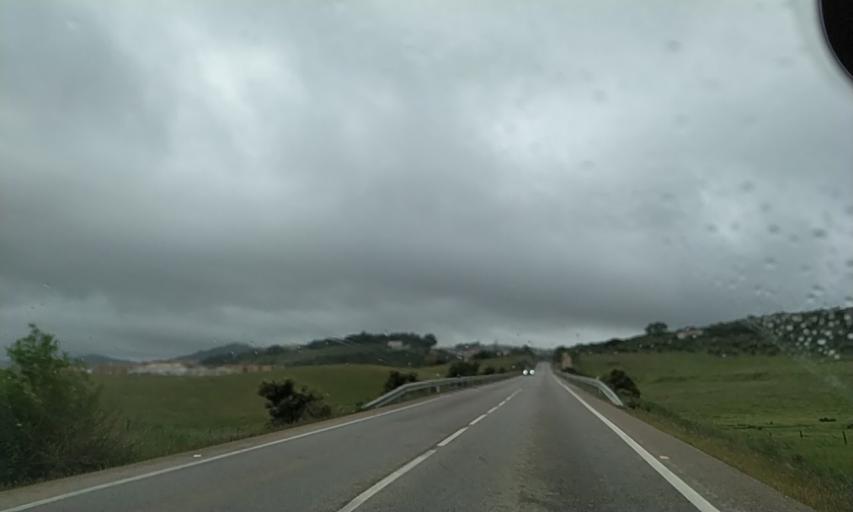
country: ES
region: Extremadura
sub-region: Provincia de Caceres
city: Caceres
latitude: 39.4931
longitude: -6.3850
